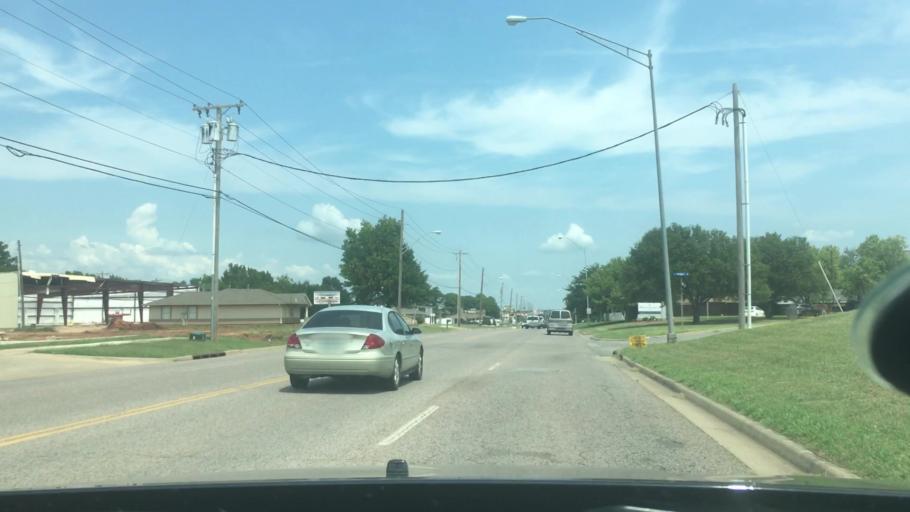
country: US
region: Oklahoma
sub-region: Pottawatomie County
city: Shawnee
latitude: 35.3708
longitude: -96.9297
